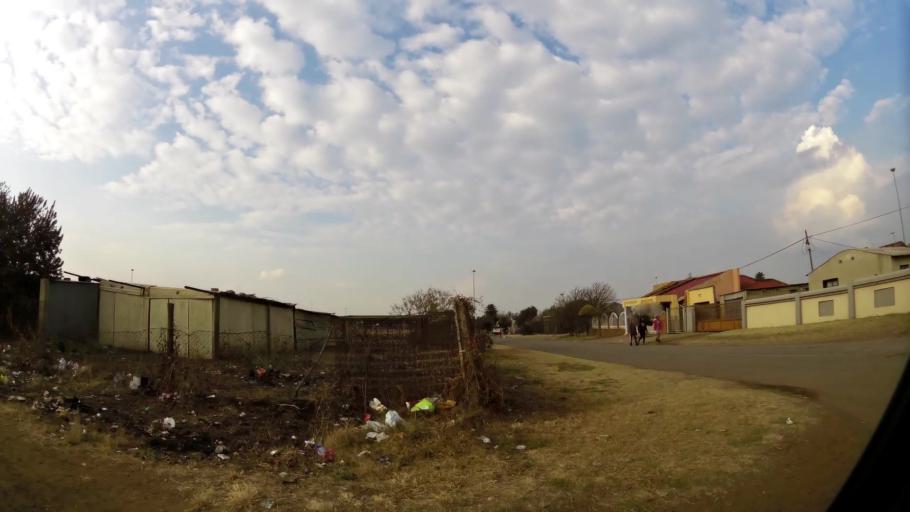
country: ZA
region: Gauteng
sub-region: Sedibeng District Municipality
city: Vanderbijlpark
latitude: -26.6832
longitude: 27.8725
